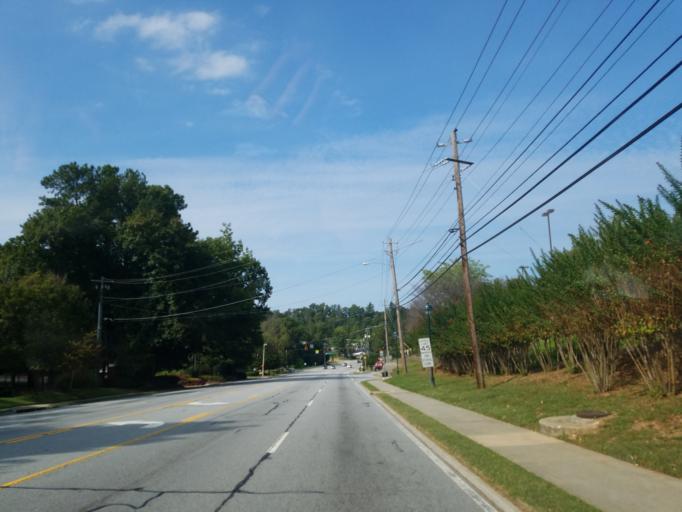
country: US
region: Georgia
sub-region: DeKalb County
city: Dunwoody
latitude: 33.9589
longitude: -84.3651
